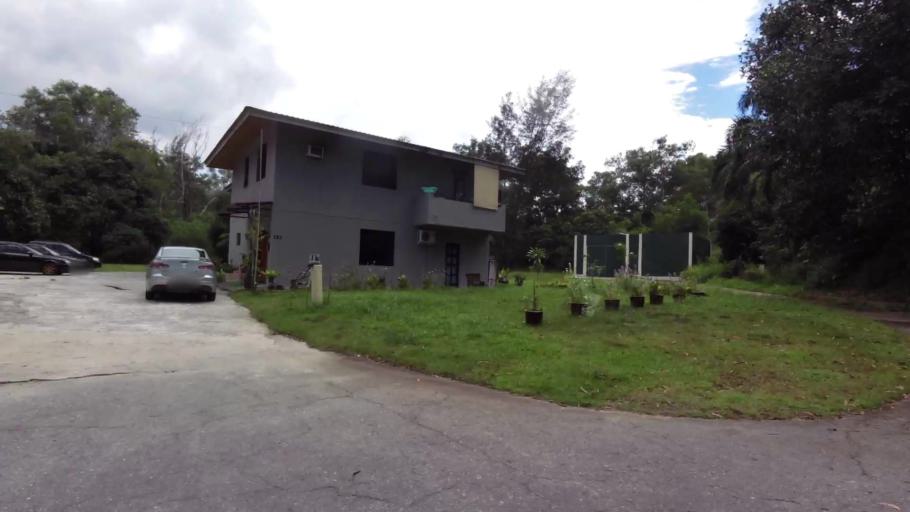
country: BN
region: Brunei and Muara
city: Bandar Seri Begawan
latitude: 4.9845
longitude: 114.9300
